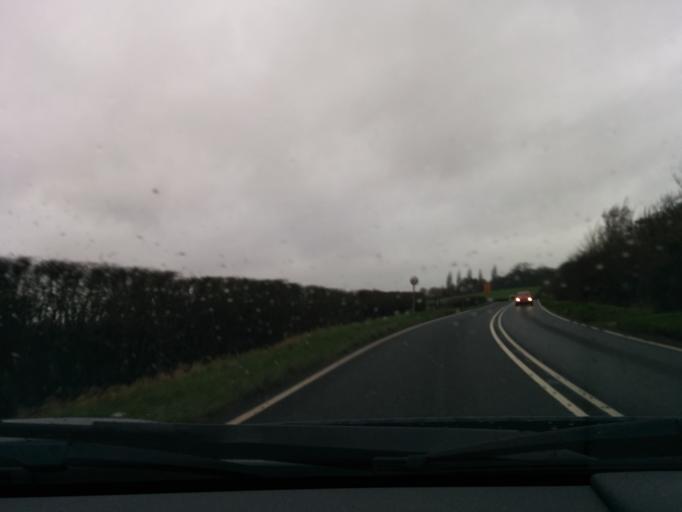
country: GB
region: England
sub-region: Oxfordshire
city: Boars Hill
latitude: 51.7524
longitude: -1.3258
